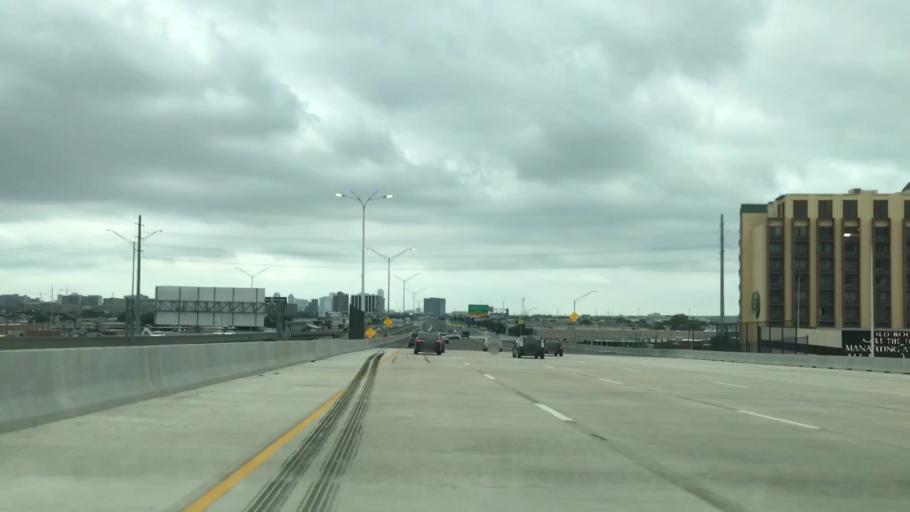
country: US
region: Texas
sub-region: Dallas County
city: Irving
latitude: 32.8290
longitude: -96.8885
